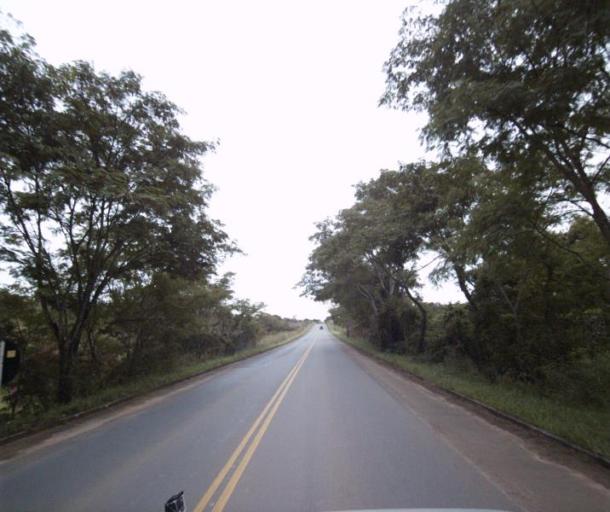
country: BR
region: Goias
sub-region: Pirenopolis
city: Pirenopolis
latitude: -15.8725
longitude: -48.7835
